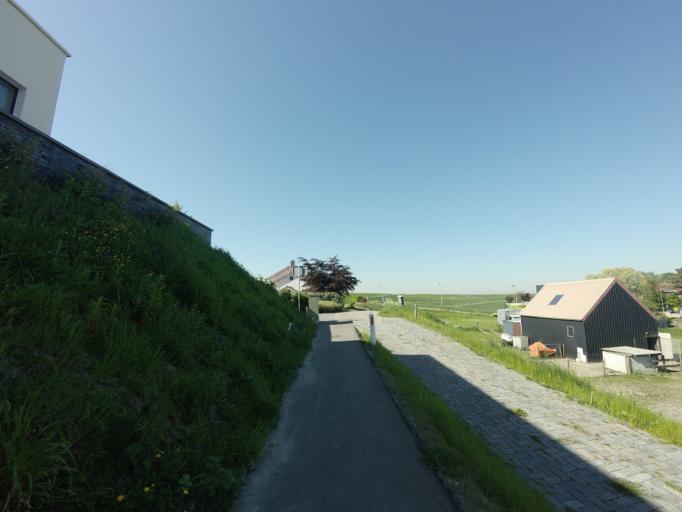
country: NL
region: North Brabant
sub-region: Gemeente Woensdrecht
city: Woensdrecht
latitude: 51.4017
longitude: 4.2128
